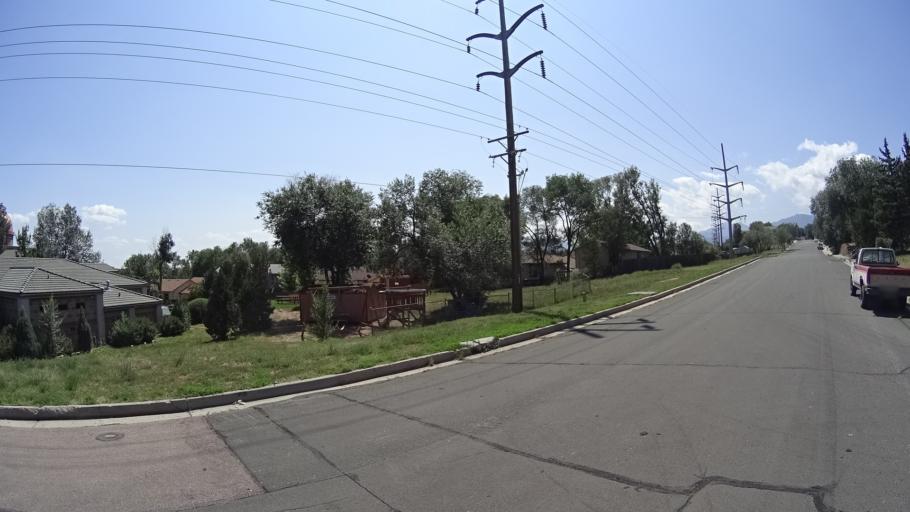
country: US
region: Colorado
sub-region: El Paso County
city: Colorado Springs
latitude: 38.8718
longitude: -104.8369
